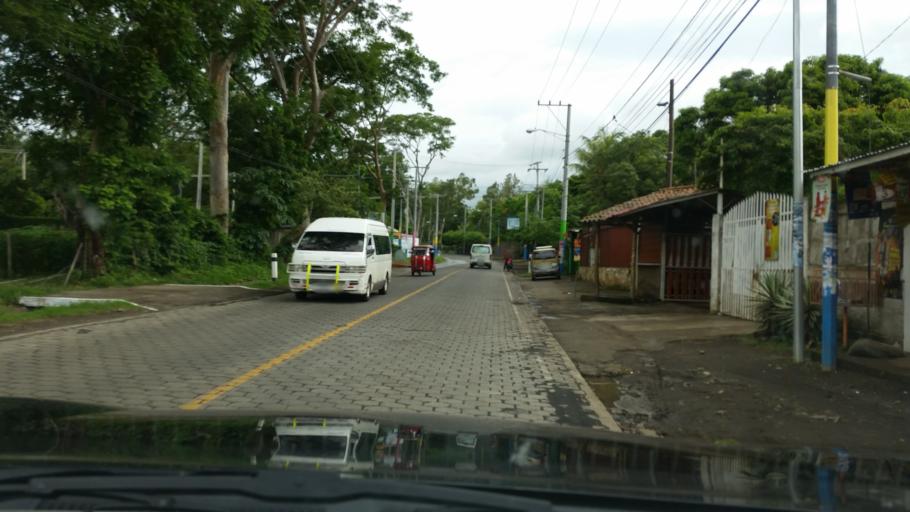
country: NI
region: Masaya
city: Ticuantepe
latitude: 12.0342
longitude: -86.2058
